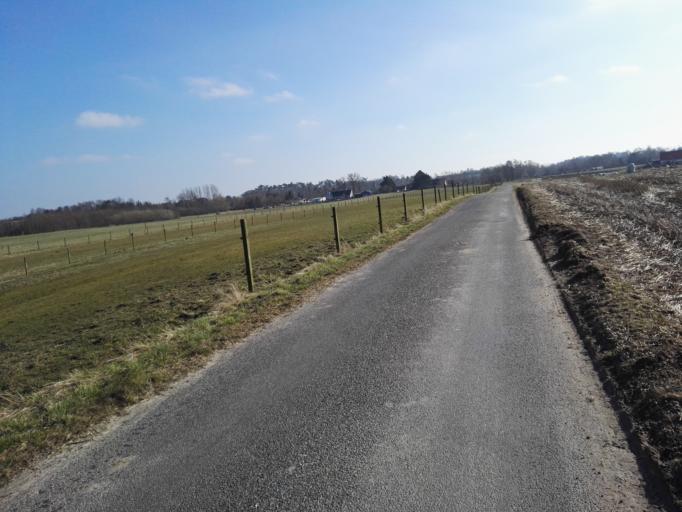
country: DK
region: Capital Region
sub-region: Frederikssund Kommune
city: Frederikssund
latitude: 55.7899
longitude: 12.0294
